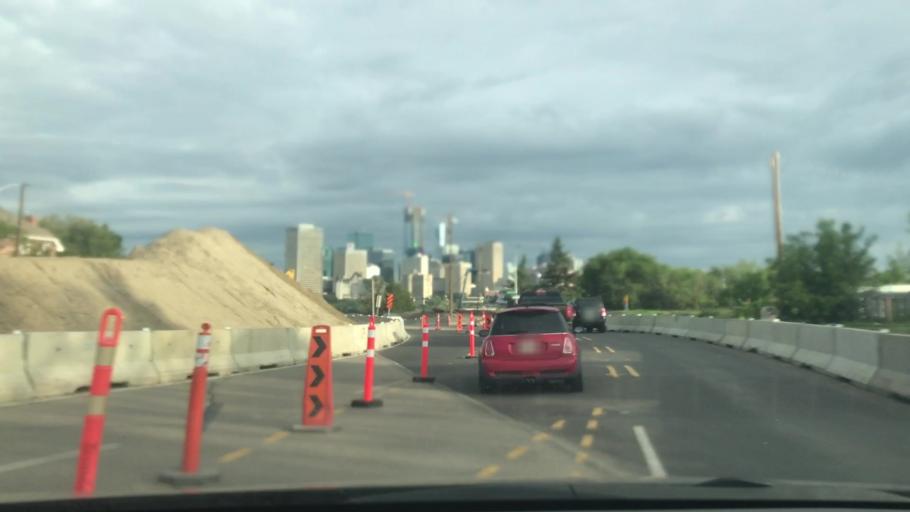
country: CA
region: Alberta
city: Edmonton
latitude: 53.5320
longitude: -113.4721
